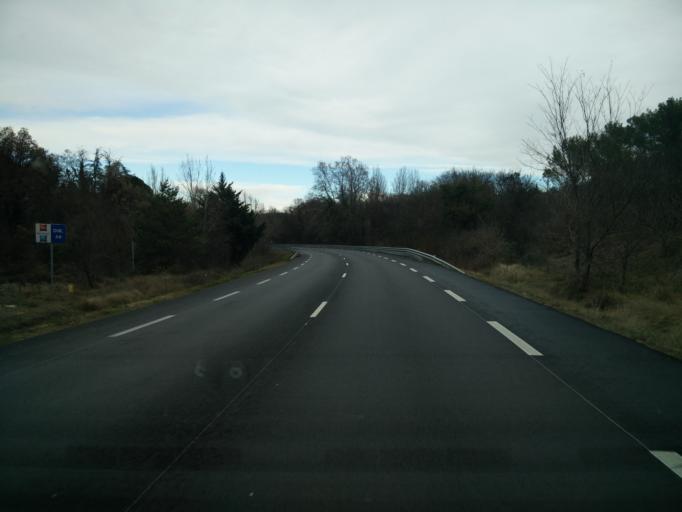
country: FR
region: Provence-Alpes-Cote d'Azur
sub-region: Departement du Var
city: La Celle
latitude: 43.3923
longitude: 6.0462
